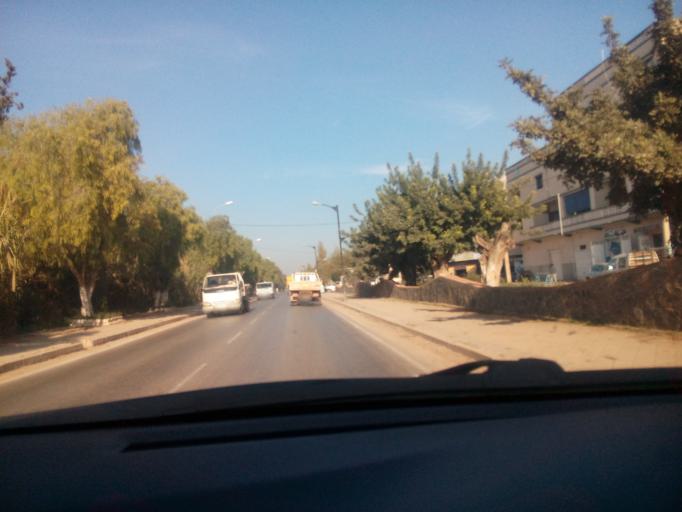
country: DZ
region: Oran
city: Es Senia
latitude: 35.6400
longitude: -0.6291
